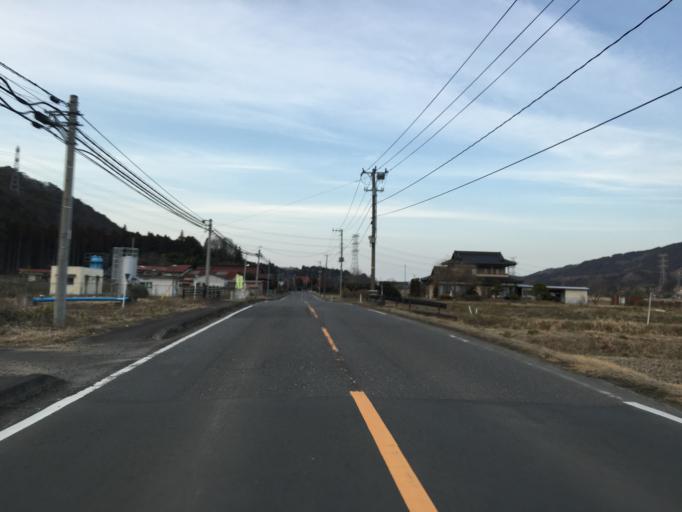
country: JP
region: Ibaraki
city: Daigo
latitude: 36.9186
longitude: 140.4081
